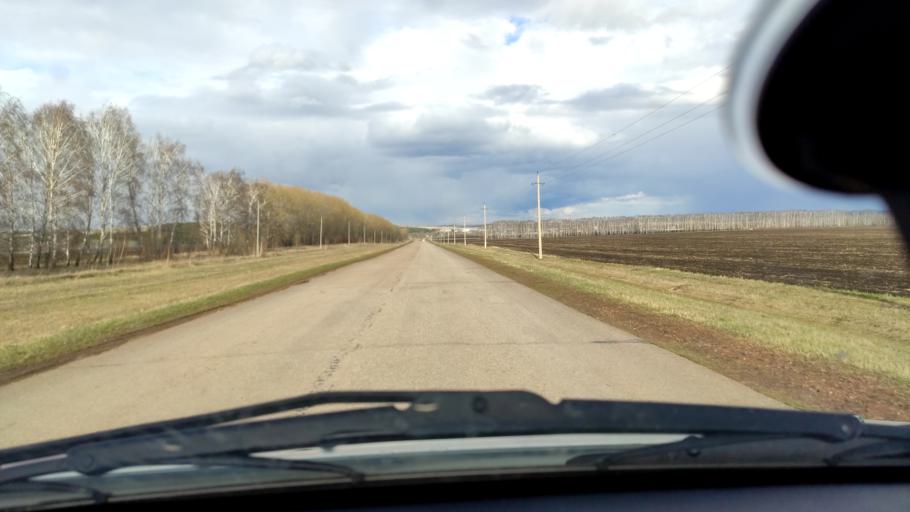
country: RU
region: Bashkortostan
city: Buzdyak
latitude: 54.7606
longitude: 54.5703
